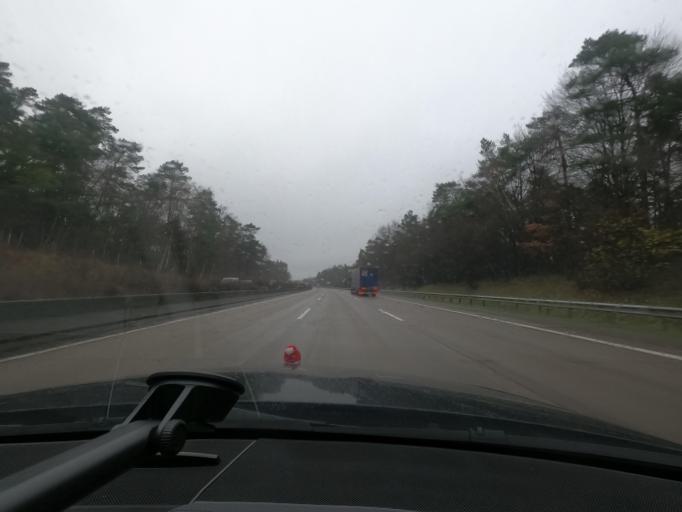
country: DE
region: Lower Saxony
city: Garlstorf
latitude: 53.2584
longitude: 10.0884
